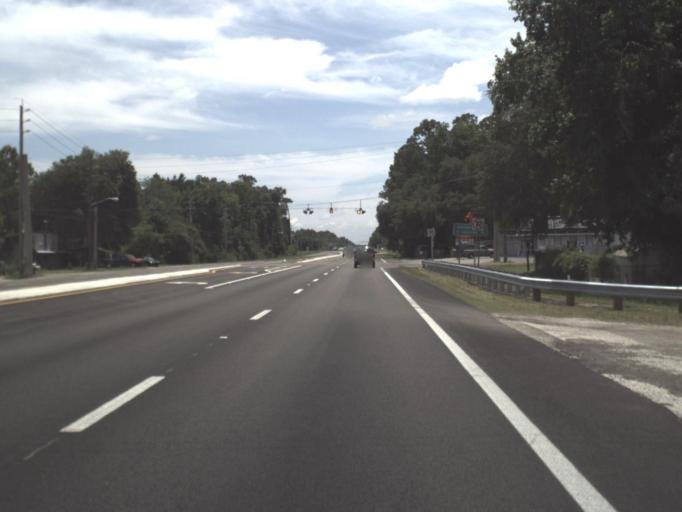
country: US
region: Florida
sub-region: Nassau County
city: Nassau Village-Ratliff
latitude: 30.4371
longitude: -81.7629
